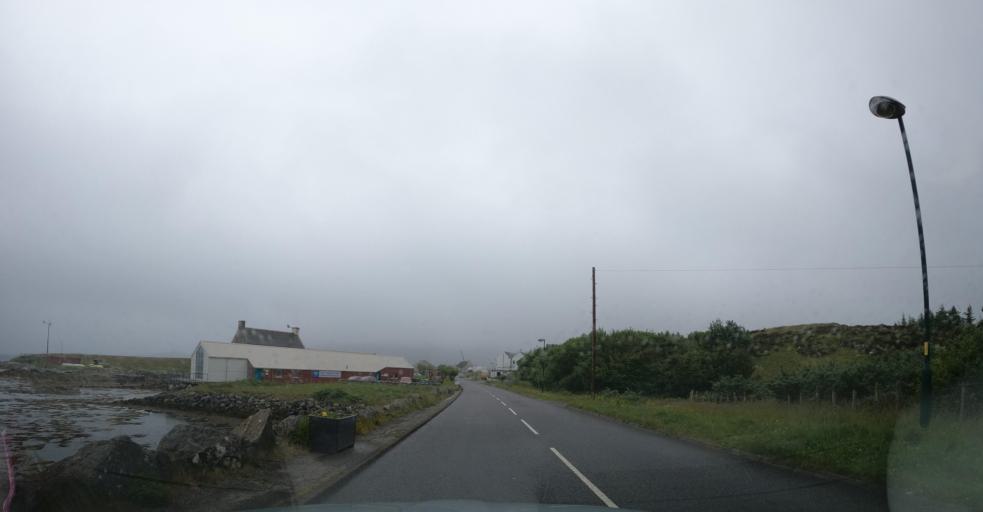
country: GB
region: Scotland
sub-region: Eilean Siar
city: Isle of North Uist
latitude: 57.5993
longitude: -7.1601
